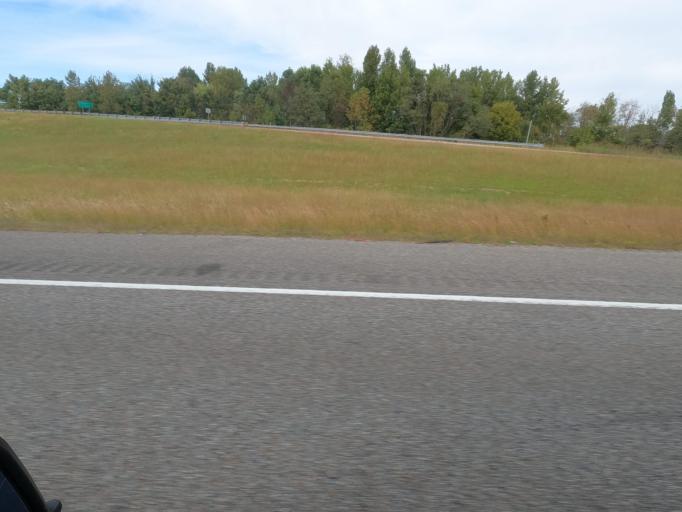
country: US
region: Tennessee
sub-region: Haywood County
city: Brownsville
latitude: 35.5572
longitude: -89.1889
